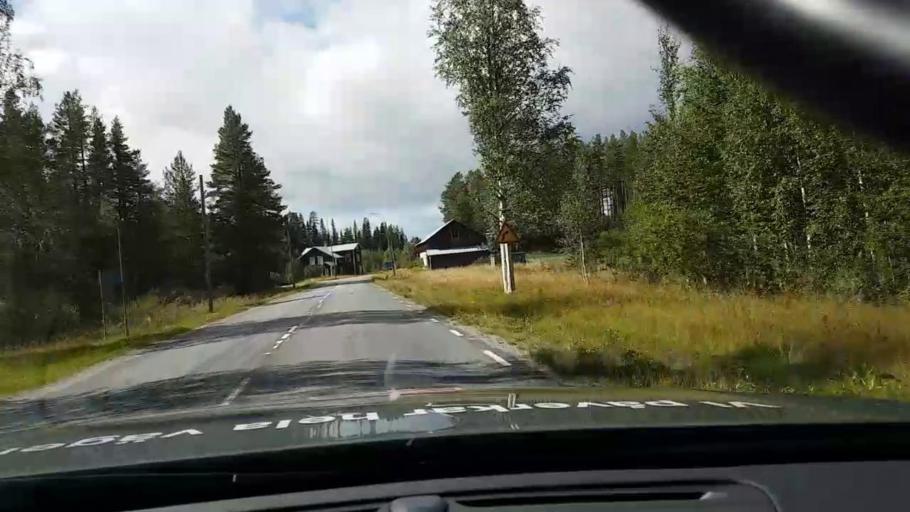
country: SE
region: Vaesterbotten
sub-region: Asele Kommun
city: Asele
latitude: 63.8602
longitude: 17.3769
